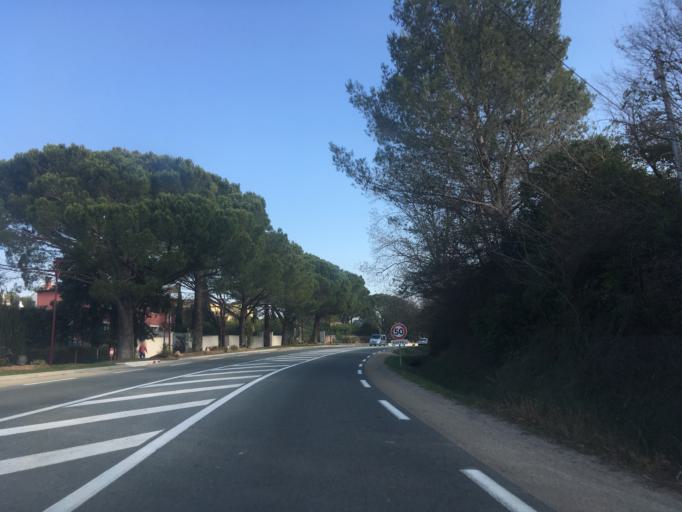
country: FR
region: Provence-Alpes-Cote d'Azur
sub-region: Departement du Var
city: Vidauban
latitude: 43.4332
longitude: 6.4385
